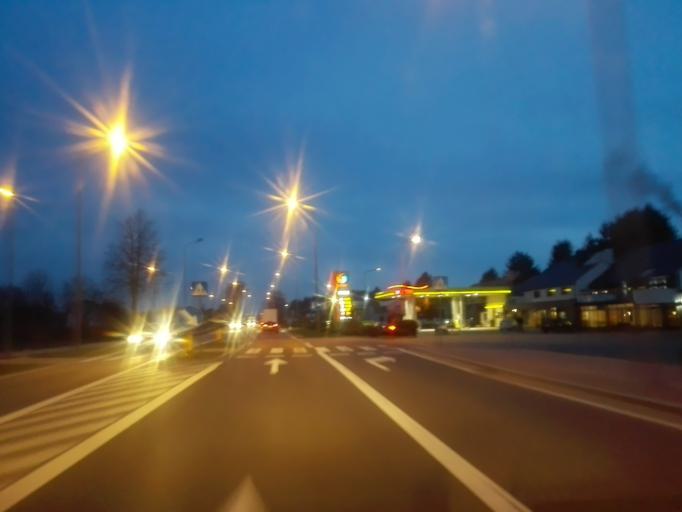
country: PL
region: Podlasie
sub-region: Lomza
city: Lomza
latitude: 53.1486
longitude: 22.0475
